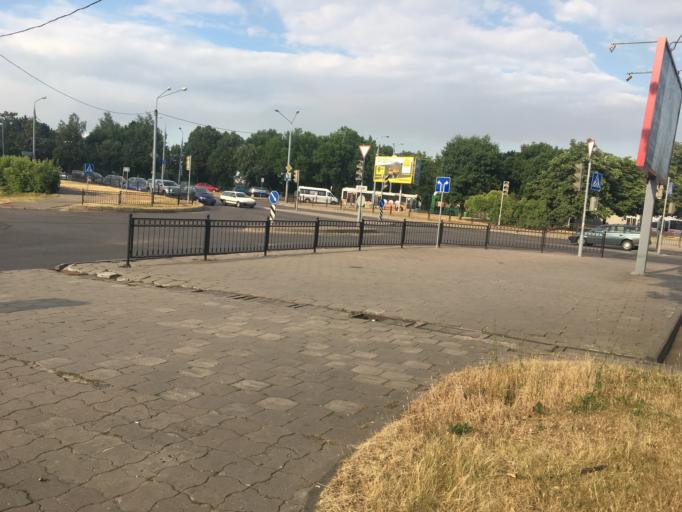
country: BY
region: Grodnenskaya
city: Hrodna
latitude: 53.6619
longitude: 23.8298
